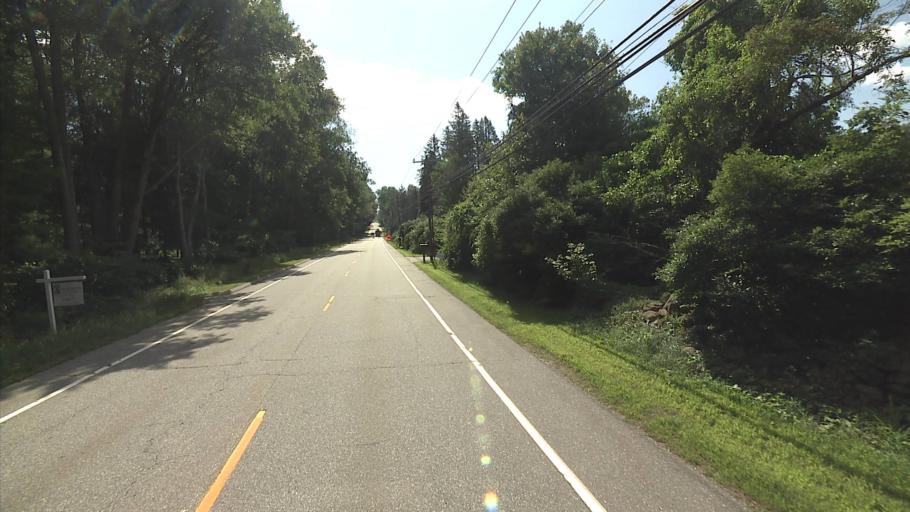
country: US
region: Connecticut
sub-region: Tolland County
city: Stafford Springs
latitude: 41.9554
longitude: -72.2797
